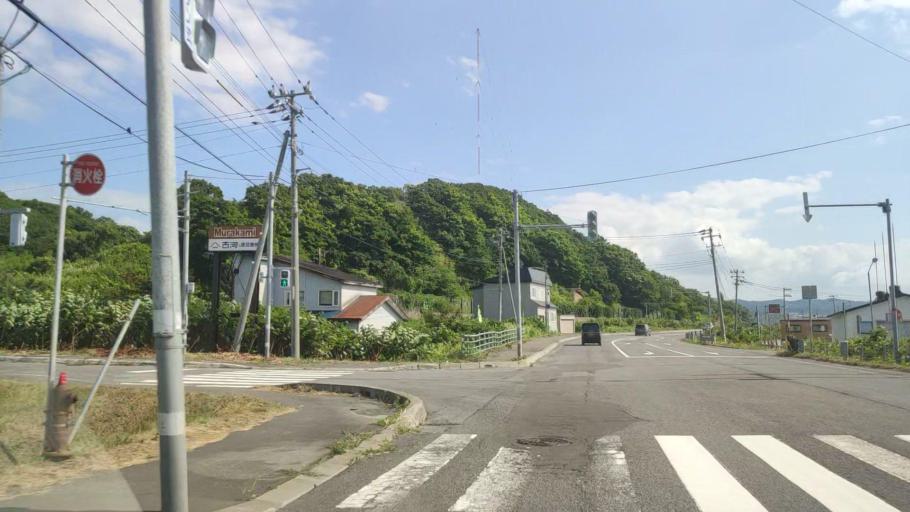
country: JP
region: Hokkaido
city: Rumoi
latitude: 43.9586
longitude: 141.6440
